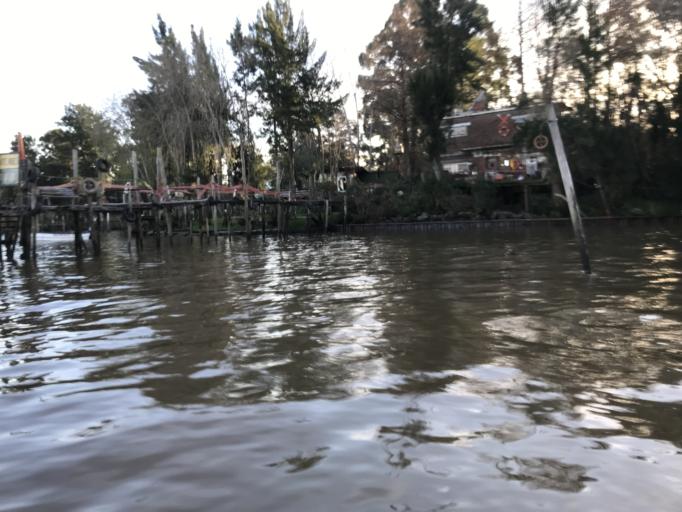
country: AR
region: Buenos Aires
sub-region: Partido de Tigre
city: Tigre
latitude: -34.3808
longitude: -58.5745
